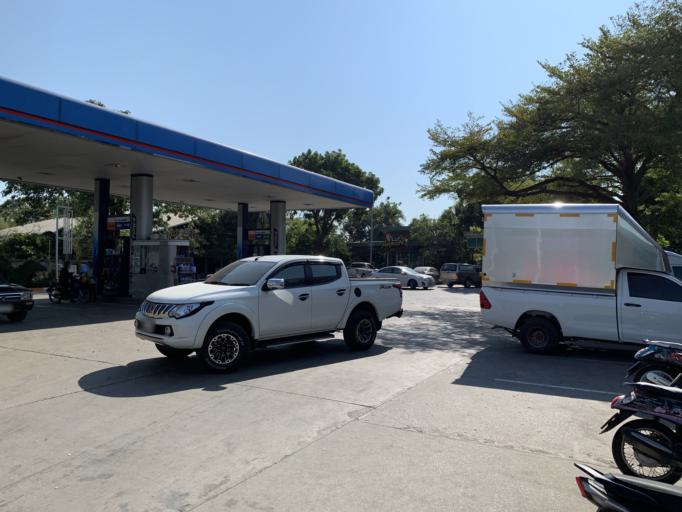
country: TH
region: Phra Nakhon Si Ayutthaya
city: Phachi
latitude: 14.4447
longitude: 100.7186
